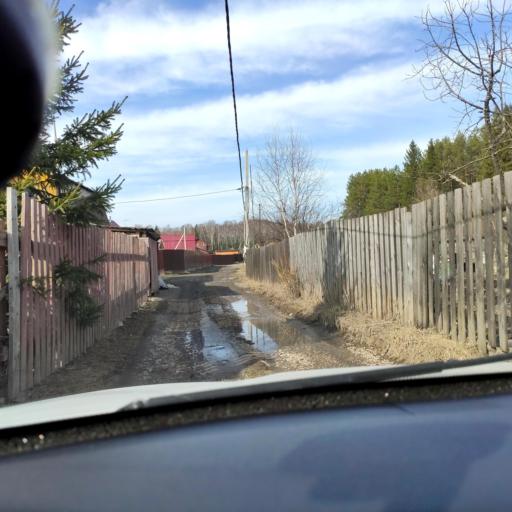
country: RU
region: Perm
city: Overyata
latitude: 58.0574
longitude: 55.9856
